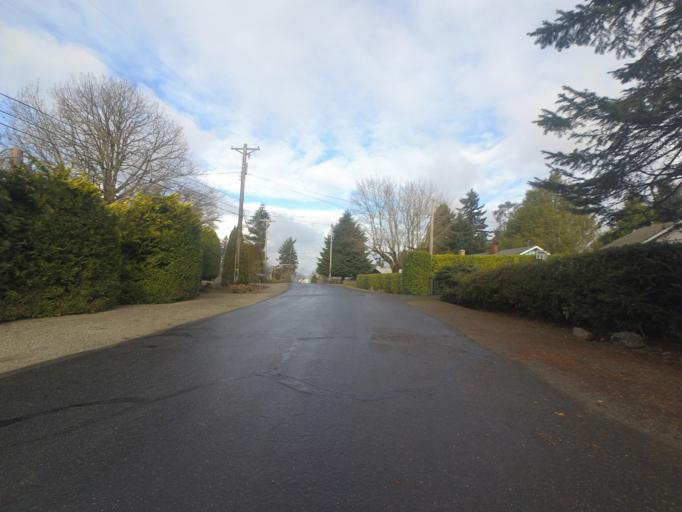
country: US
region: Washington
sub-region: Pierce County
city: University Place
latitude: 47.2269
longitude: -122.5492
